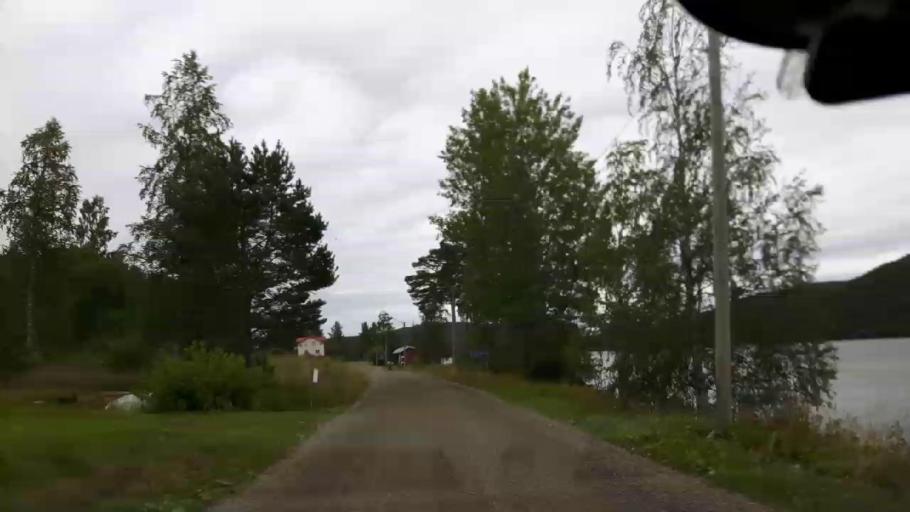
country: SE
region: Jaemtland
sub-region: Braecke Kommun
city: Braecke
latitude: 63.0025
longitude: 15.3812
